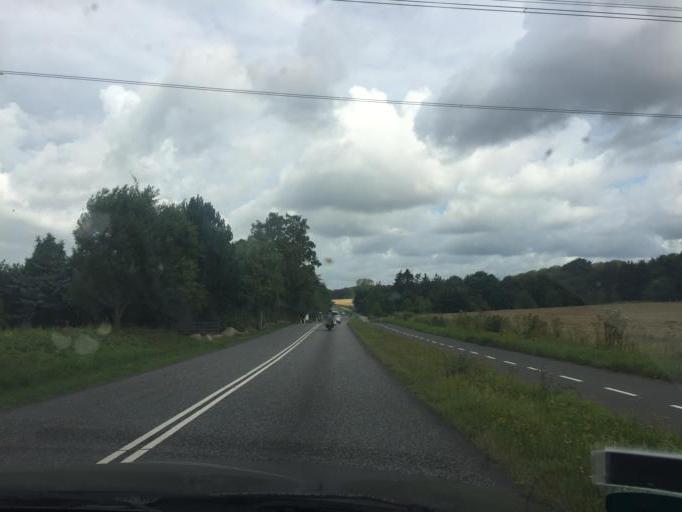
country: DK
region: Capital Region
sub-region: Allerod Kommune
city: Lillerod
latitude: 55.8939
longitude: 12.3498
